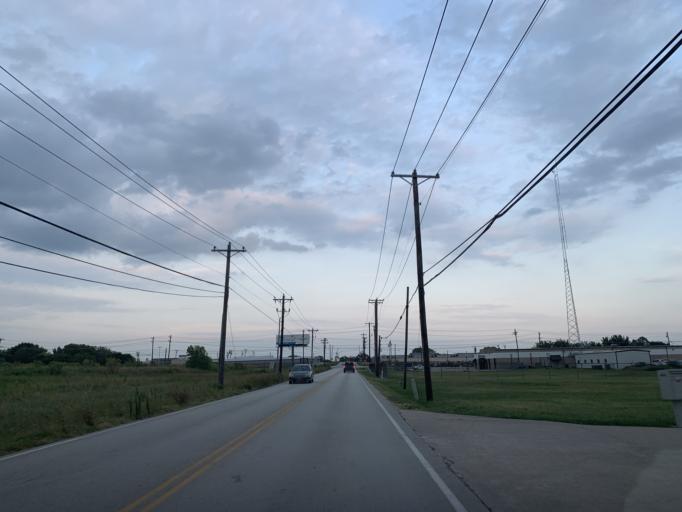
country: US
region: Texas
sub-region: Tarrant County
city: Keller
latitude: 32.9387
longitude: -97.2575
